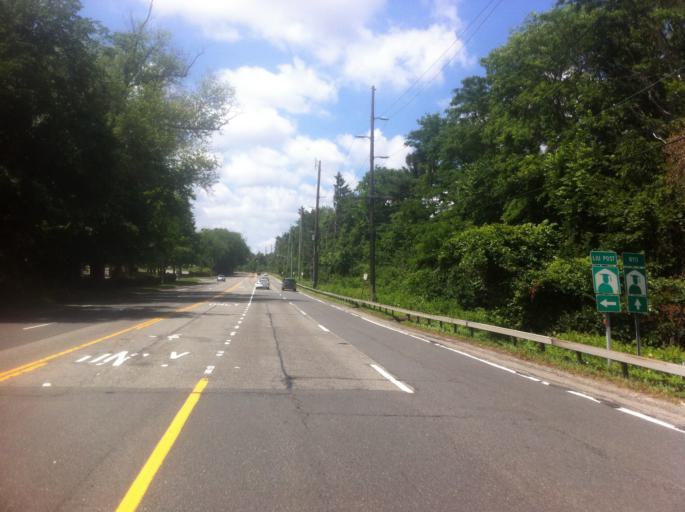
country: US
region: New York
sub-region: Nassau County
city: Old Brookville
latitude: 40.8242
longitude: -73.5909
